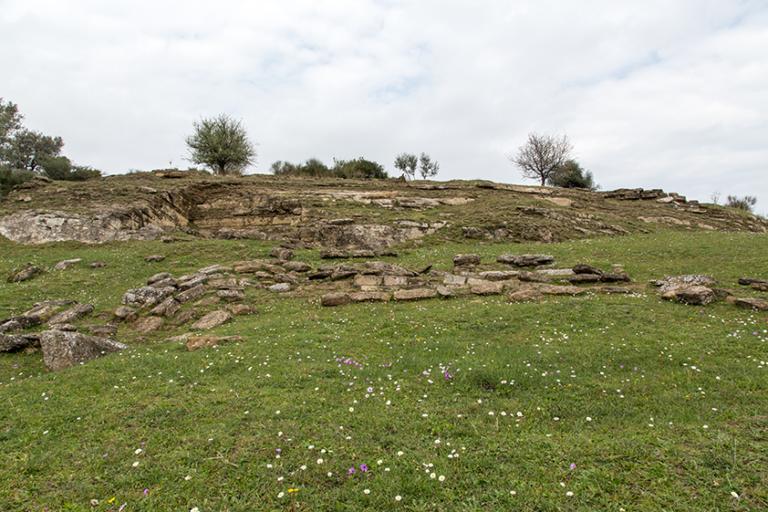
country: IT
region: Calabria
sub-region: Provincia di Cosenza
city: Paludi
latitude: 39.5415
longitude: 16.6958
